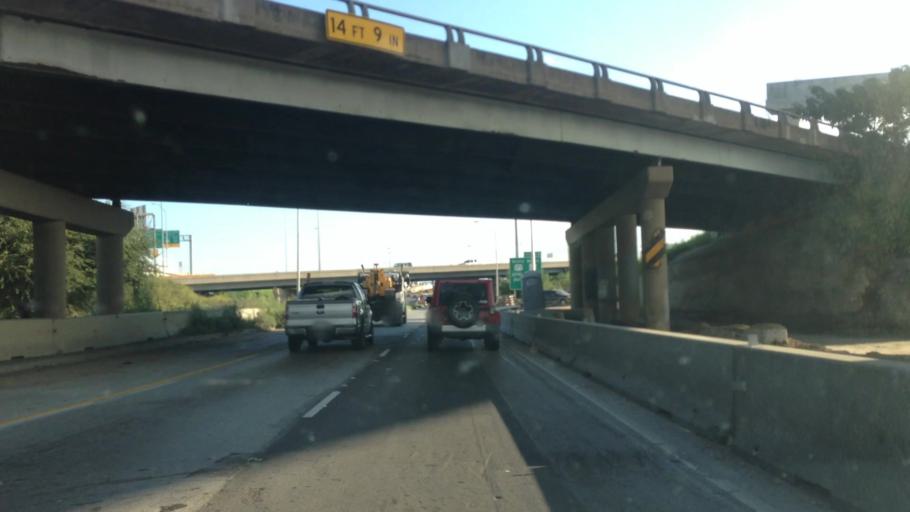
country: US
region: Texas
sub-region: Tarrant County
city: Fort Worth
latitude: 32.7656
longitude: -97.3187
